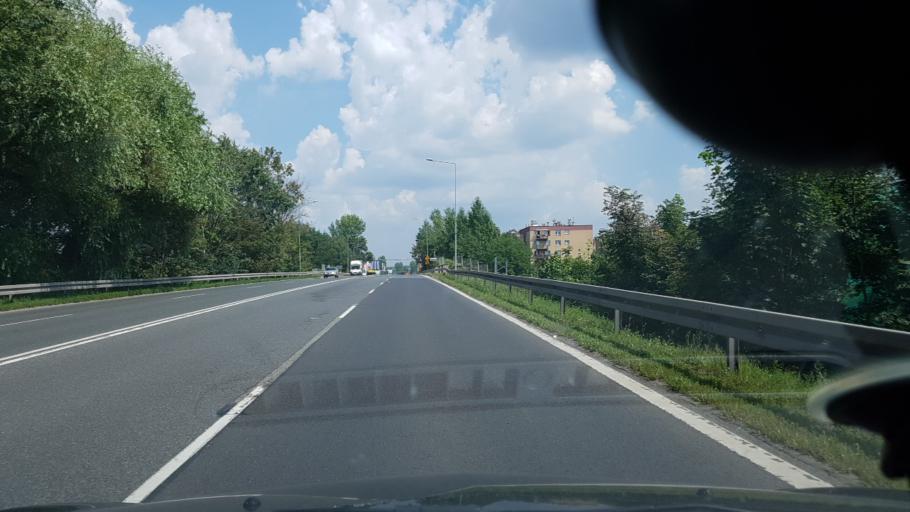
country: PL
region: Silesian Voivodeship
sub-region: Powiat mikolowski
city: Mikolow
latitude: 50.2079
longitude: 18.9612
